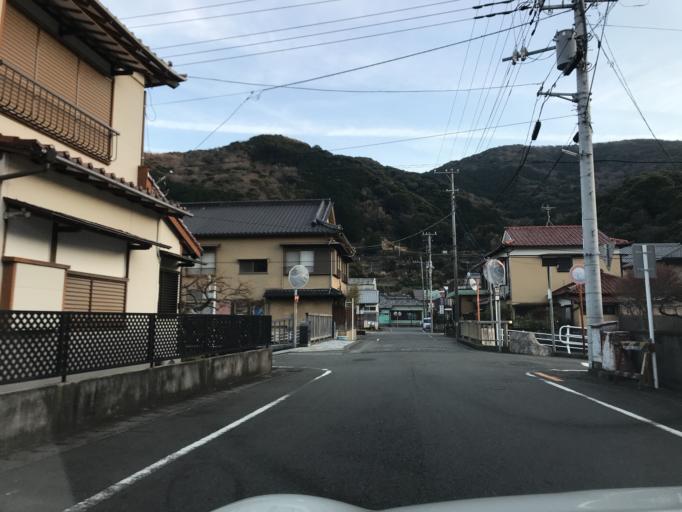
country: JP
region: Shizuoka
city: Heda
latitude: 34.9708
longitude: 138.7807
